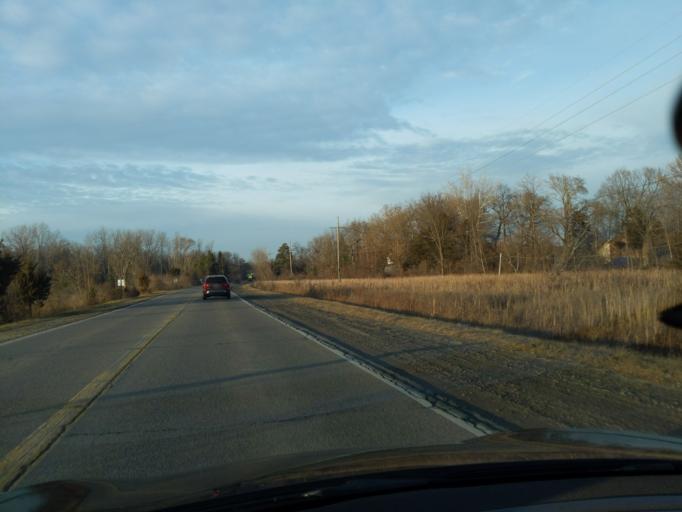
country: US
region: Michigan
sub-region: Livingston County
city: Brighton
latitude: 42.5571
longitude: -83.7546
